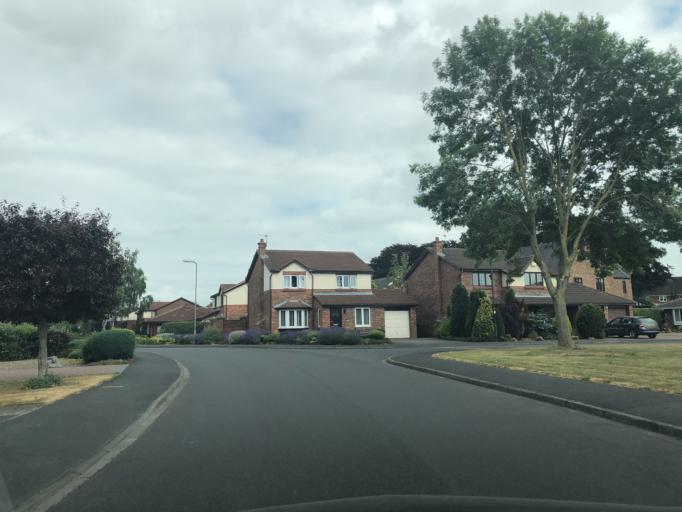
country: GB
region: England
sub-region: North Yorkshire
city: Stokesley
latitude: 54.4742
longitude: -1.1896
